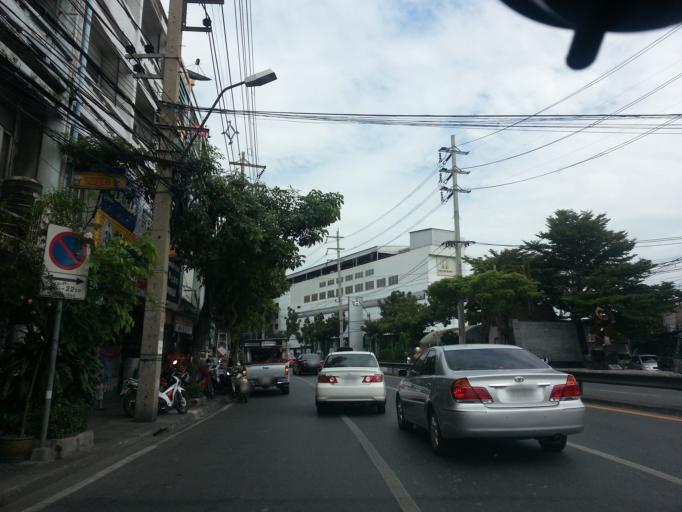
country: TH
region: Bangkok
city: Khlong Toei
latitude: 13.7190
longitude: 100.5623
